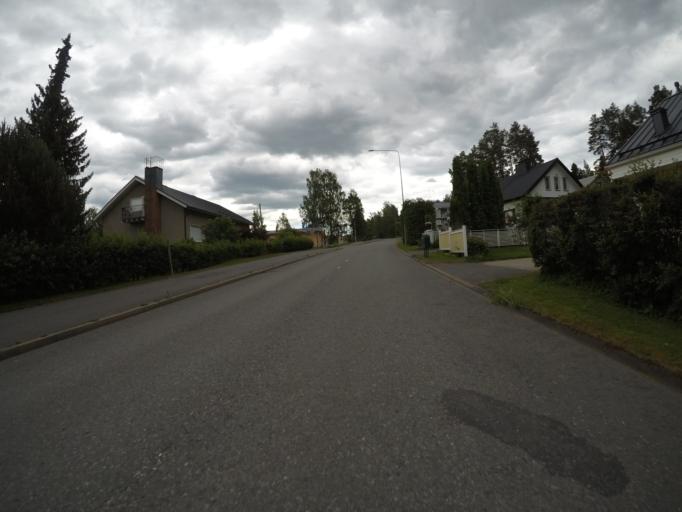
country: FI
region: Haeme
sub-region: Haemeenlinna
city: Haemeenlinna
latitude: 60.9859
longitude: 24.4346
